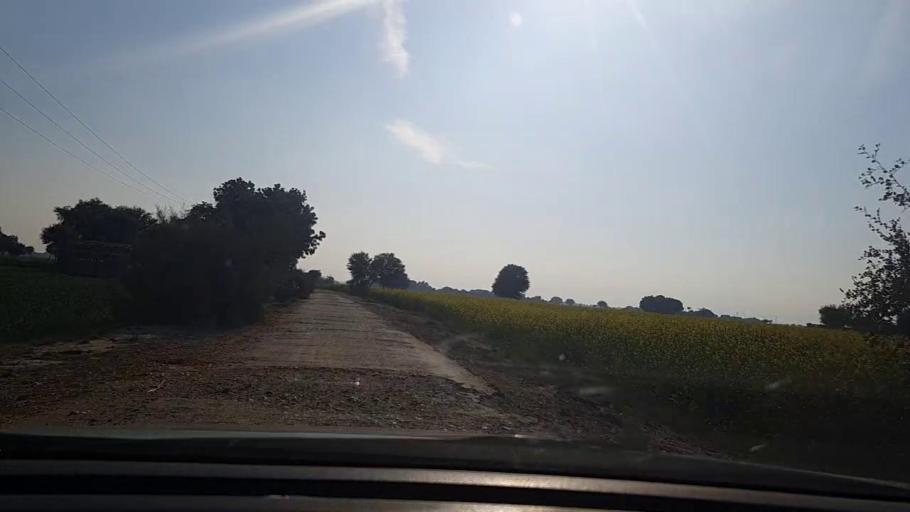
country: PK
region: Sindh
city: Sehwan
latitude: 26.3160
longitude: 68.0041
